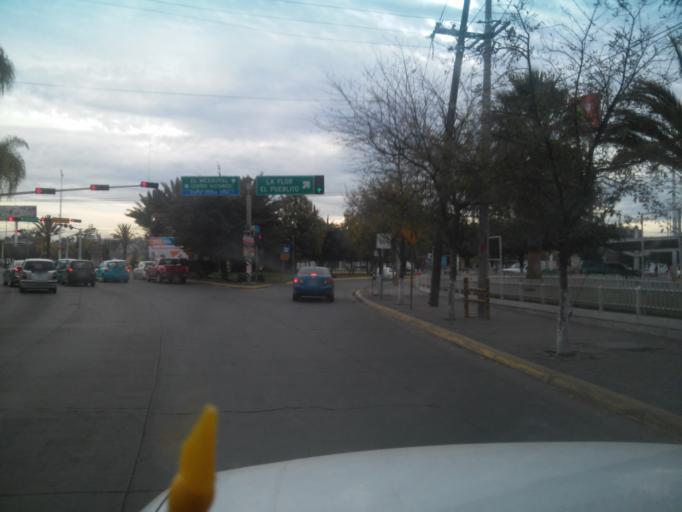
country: MX
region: Durango
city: Victoria de Durango
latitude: 24.0090
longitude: -104.6633
